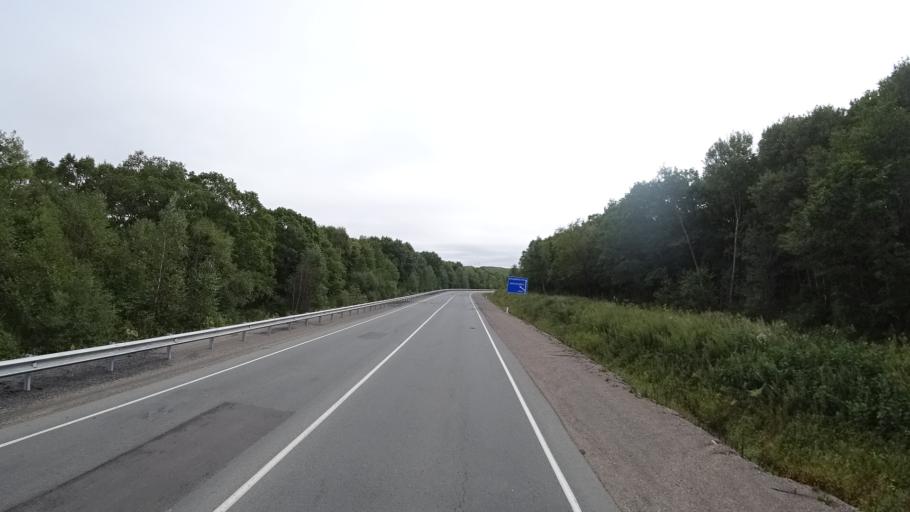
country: RU
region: Primorskiy
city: Lyalichi
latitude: 44.1052
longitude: 132.4224
